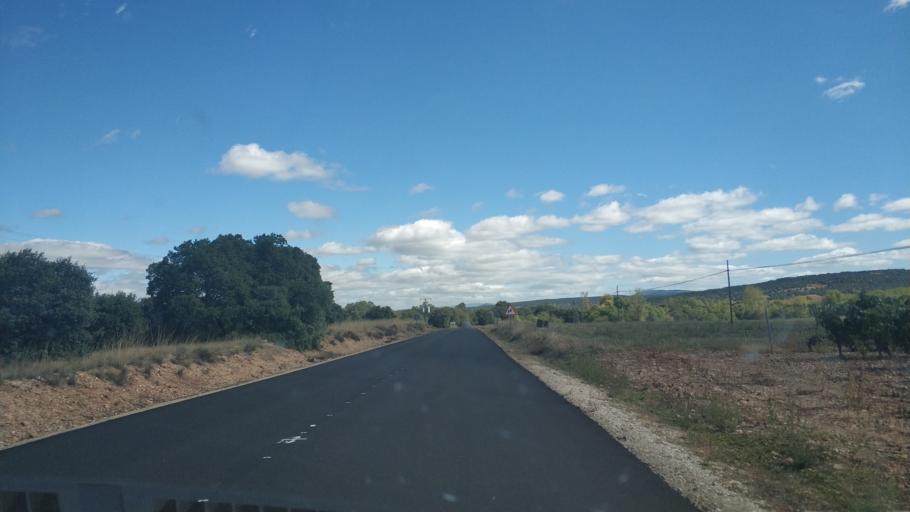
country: ES
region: Castille and Leon
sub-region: Provincia de Burgos
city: Puentedura
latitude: 42.0336
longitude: -3.6240
